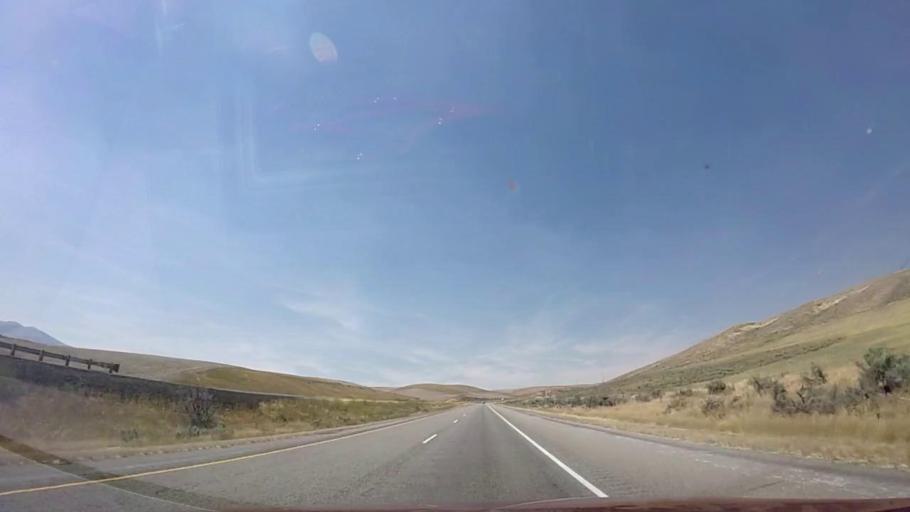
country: US
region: Idaho
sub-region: Power County
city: American Falls
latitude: 42.1839
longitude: -113.0153
